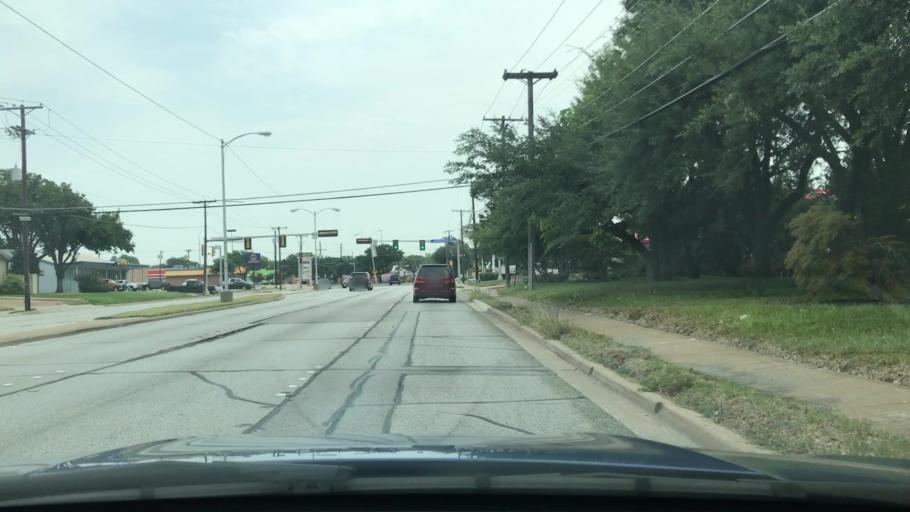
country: US
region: Texas
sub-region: Dallas County
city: Richardson
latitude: 32.9630
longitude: -96.7394
